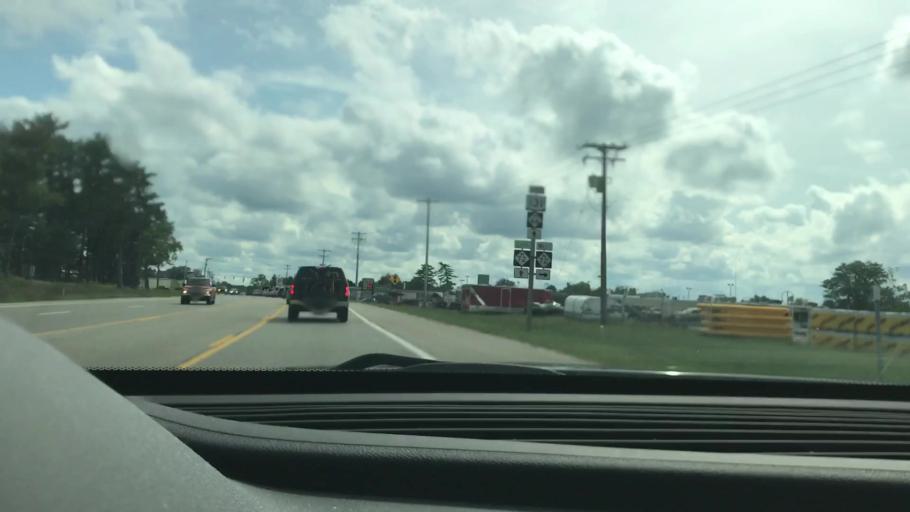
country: US
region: Michigan
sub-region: Kalkaska County
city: Kalkaska
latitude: 44.7461
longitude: -85.1742
